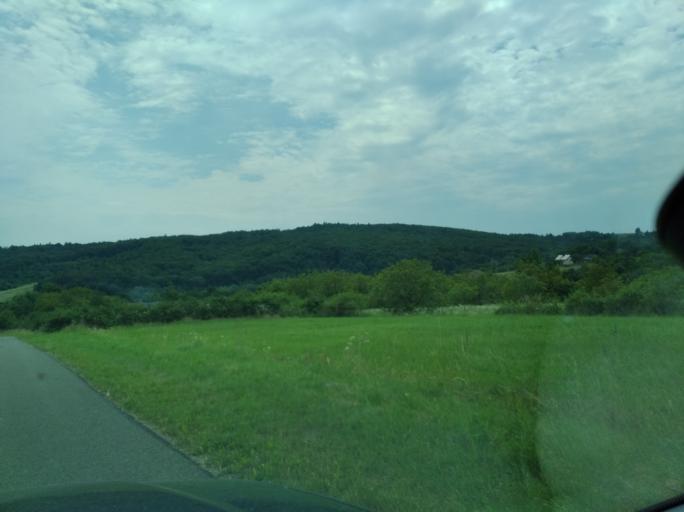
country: PL
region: Subcarpathian Voivodeship
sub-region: Powiat przeworski
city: Lopuszka Wielka
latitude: 49.9006
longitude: 22.4187
